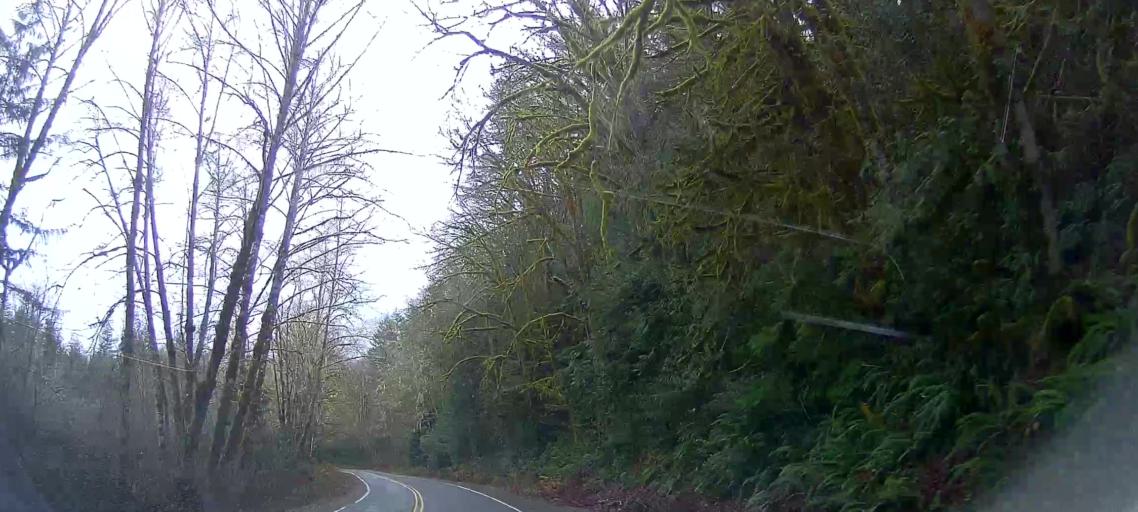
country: US
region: Washington
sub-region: Snohomish County
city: Darrington
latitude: 48.4853
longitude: -121.4889
